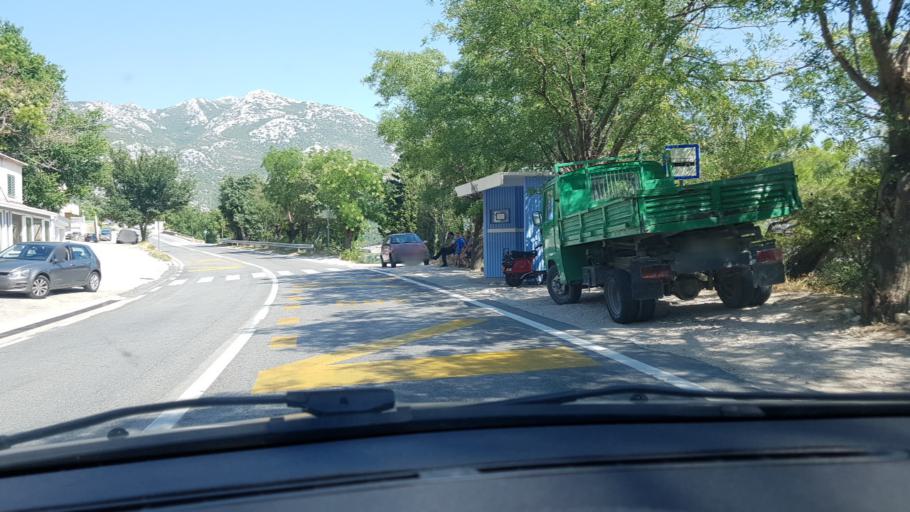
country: HR
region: Splitsko-Dalmatinska
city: Klis
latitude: 43.5581
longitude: 16.5216
